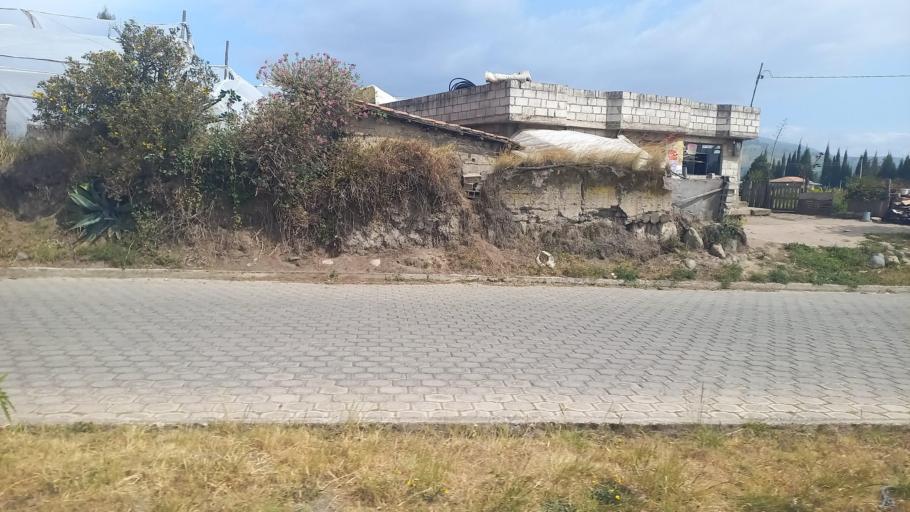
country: EC
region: Pichincha
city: Cayambe
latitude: 0.1506
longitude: -78.0685
